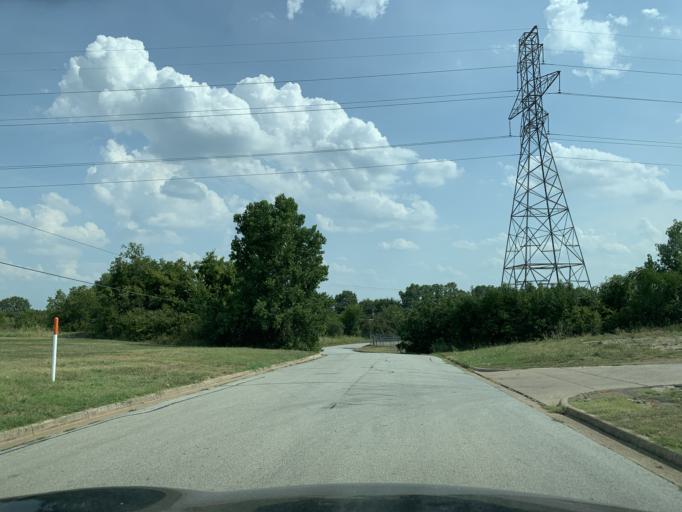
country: US
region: Texas
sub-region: Tarrant County
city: Richland Hills
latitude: 32.8083
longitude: -97.2076
